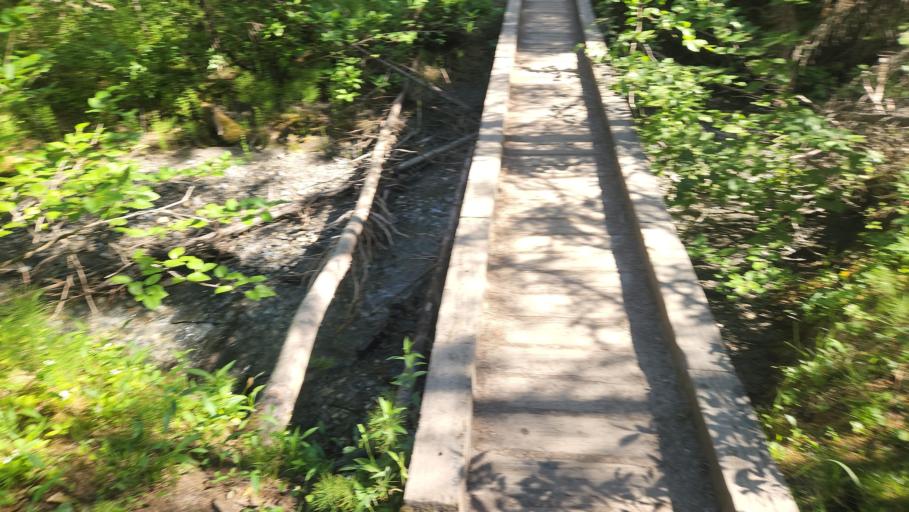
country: CA
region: Alberta
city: Lake Louise
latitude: 51.4479
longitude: -116.5257
